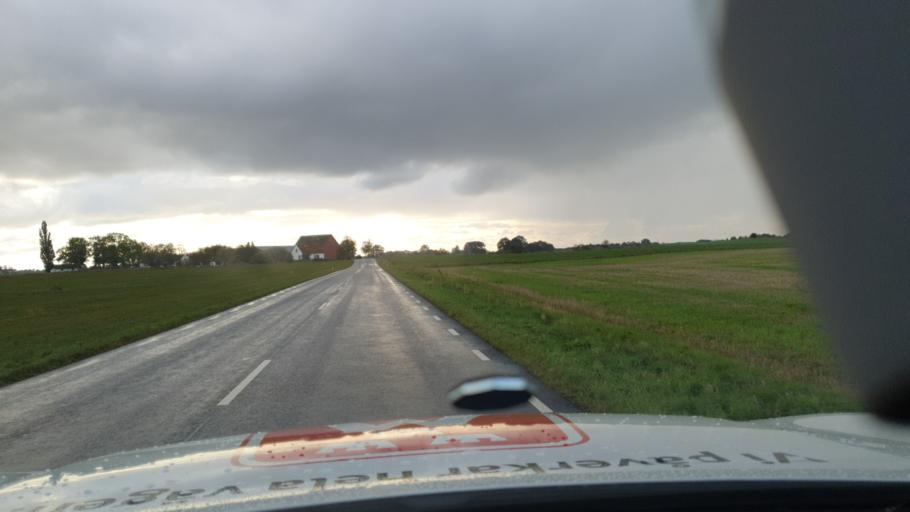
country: SE
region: Skane
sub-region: Trelleborgs Kommun
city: Anderslov
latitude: 55.4146
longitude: 13.2839
